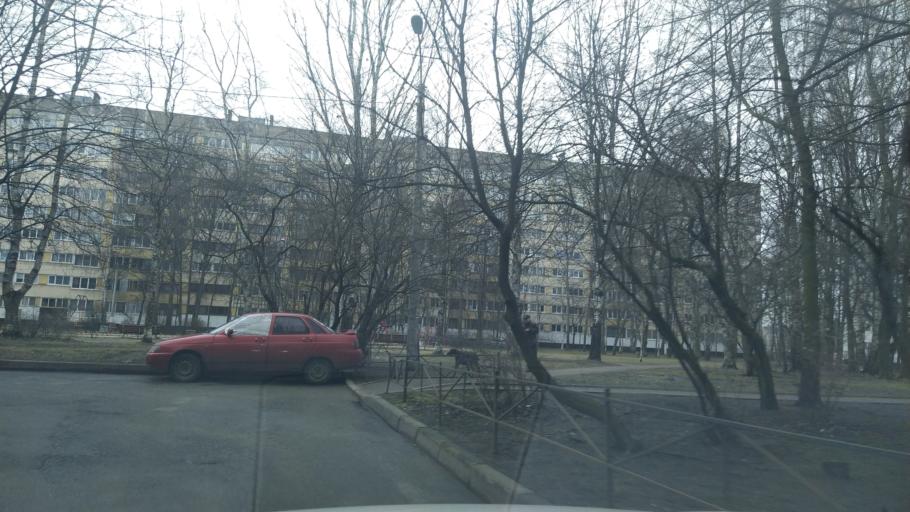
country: RU
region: St.-Petersburg
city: Grazhdanka
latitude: 60.0482
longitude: 30.3953
